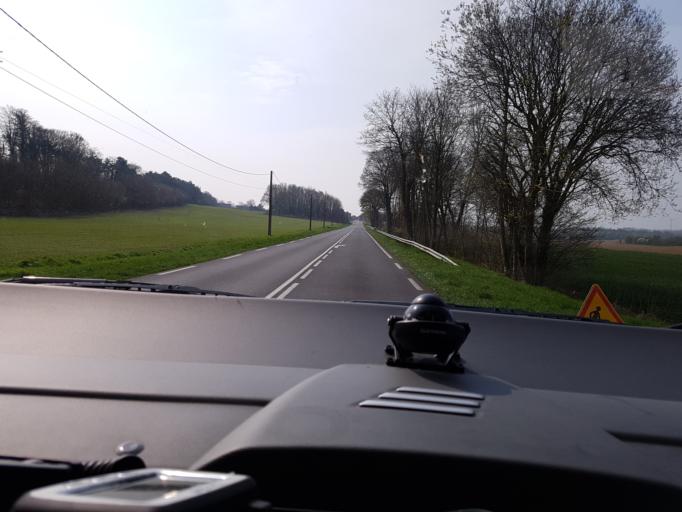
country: FR
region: Picardie
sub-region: Departement de l'Aisne
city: Beaurevoir
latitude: 49.9680
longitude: 3.2319
